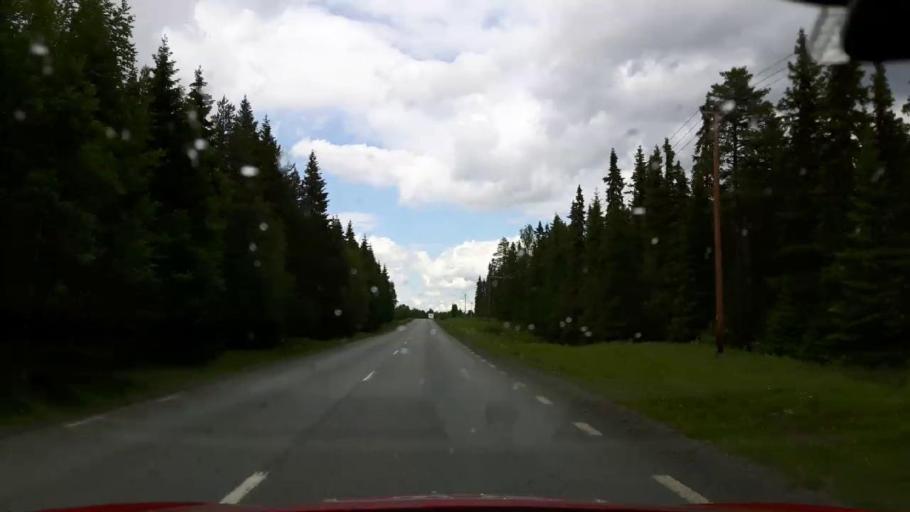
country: SE
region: Jaemtland
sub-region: Krokoms Kommun
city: Krokom
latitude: 63.5339
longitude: 14.2502
